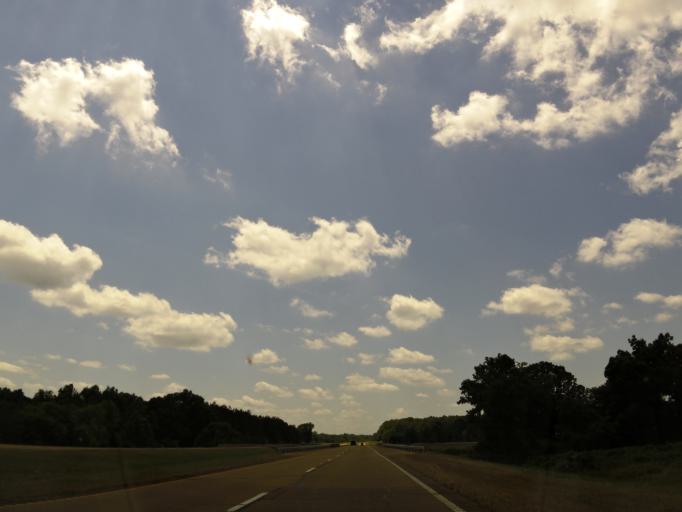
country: US
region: Mississippi
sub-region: Pontotoc County
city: Pontotoc
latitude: 34.2848
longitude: -89.1013
